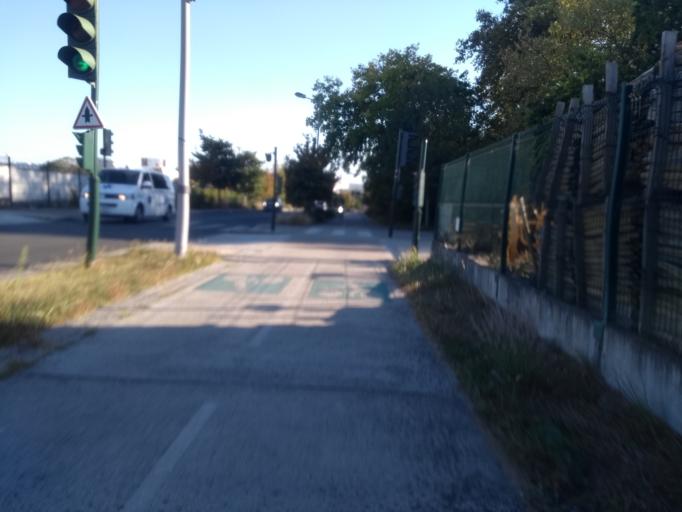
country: FR
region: Aquitaine
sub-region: Departement de la Gironde
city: Talence
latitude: 44.8110
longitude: -0.6065
